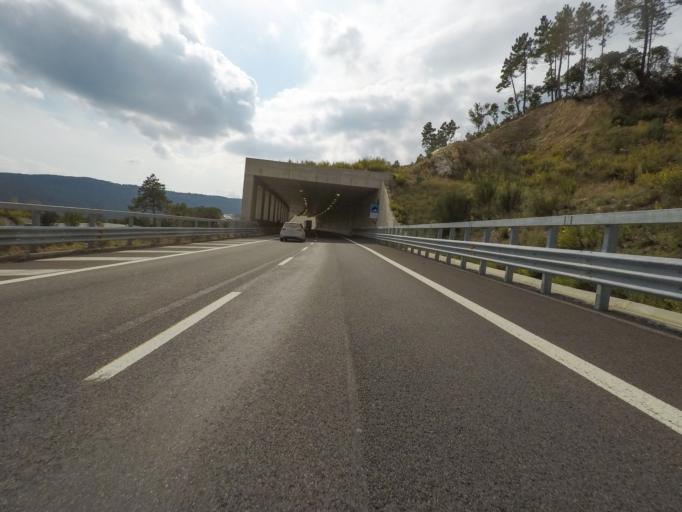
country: IT
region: Tuscany
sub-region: Provincia di Grosseto
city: Civitella Marittima
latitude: 43.0867
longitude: 11.2943
